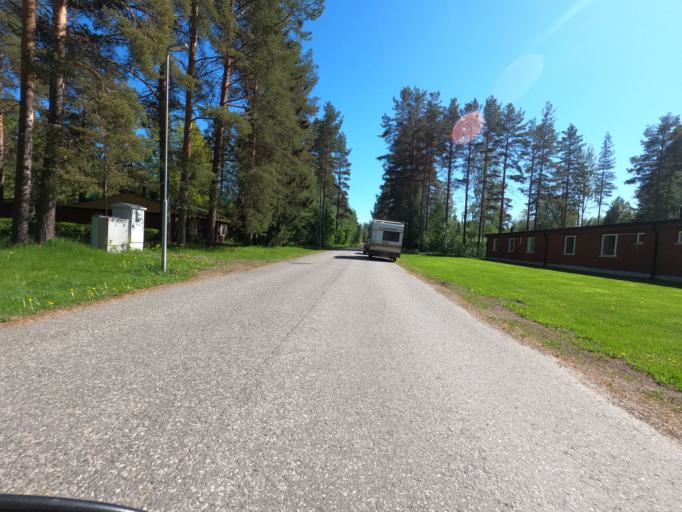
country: FI
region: North Karelia
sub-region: Joensuu
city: Joensuu
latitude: 62.5975
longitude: 29.8114
